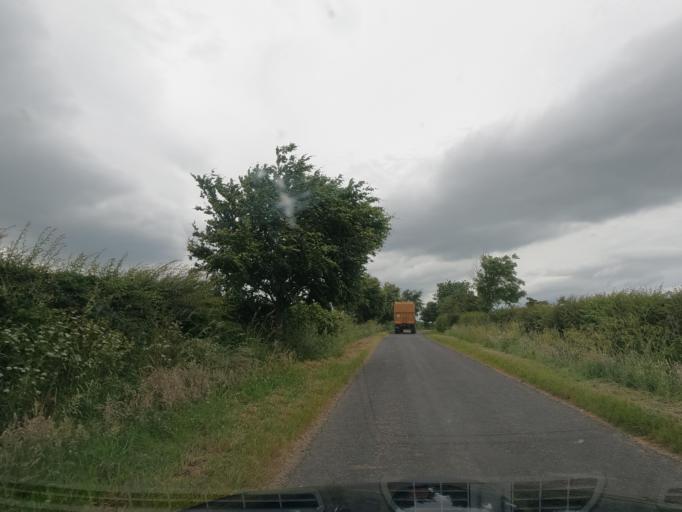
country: GB
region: England
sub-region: Northumberland
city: Lowick
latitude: 55.5743
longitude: -1.9191
